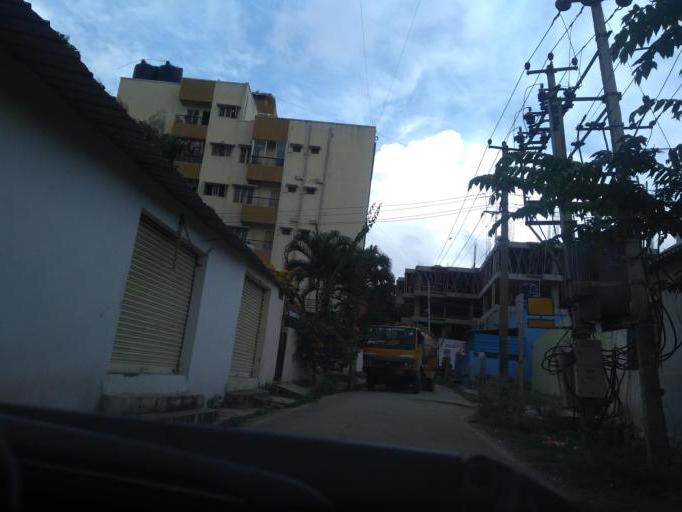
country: IN
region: Karnataka
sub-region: Bangalore Urban
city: Bangalore
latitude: 13.0089
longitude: 77.6593
